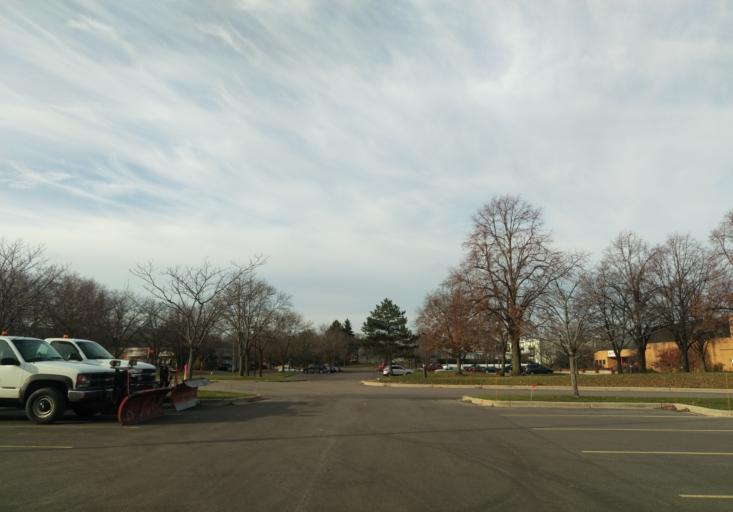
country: US
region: Wisconsin
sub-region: Dane County
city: Shorewood Hills
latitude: 43.0738
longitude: -89.4619
